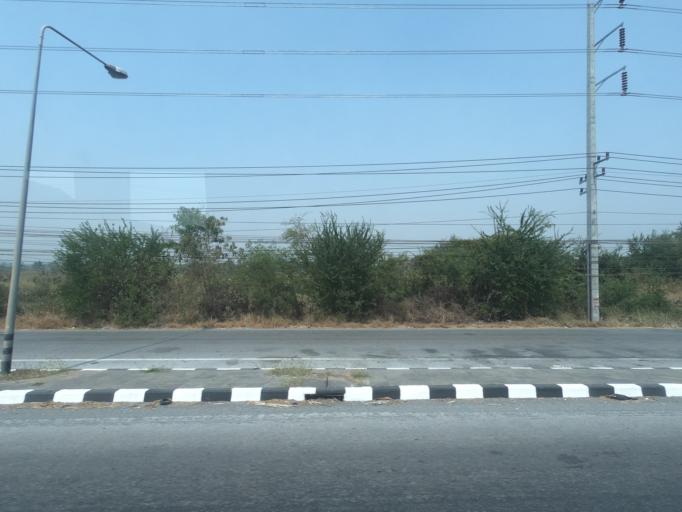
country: TH
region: Nakhon Ratchasima
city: Amphoe Sikhiu
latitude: 14.8473
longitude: 101.6361
